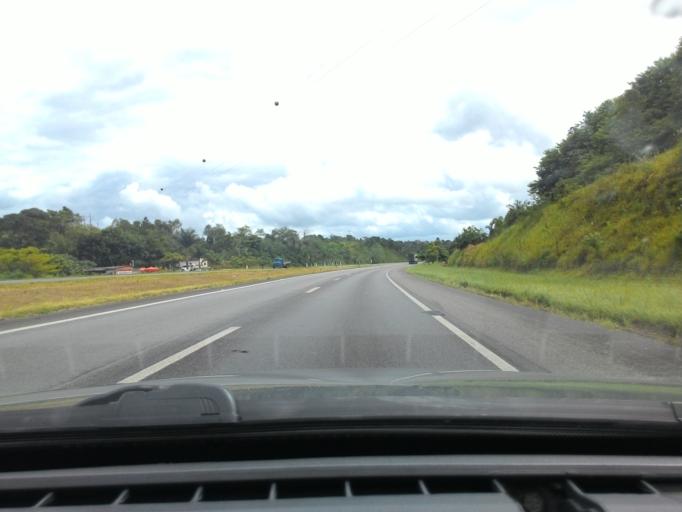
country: BR
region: Sao Paulo
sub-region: Registro
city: Registro
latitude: -24.5782
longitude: -47.8844
